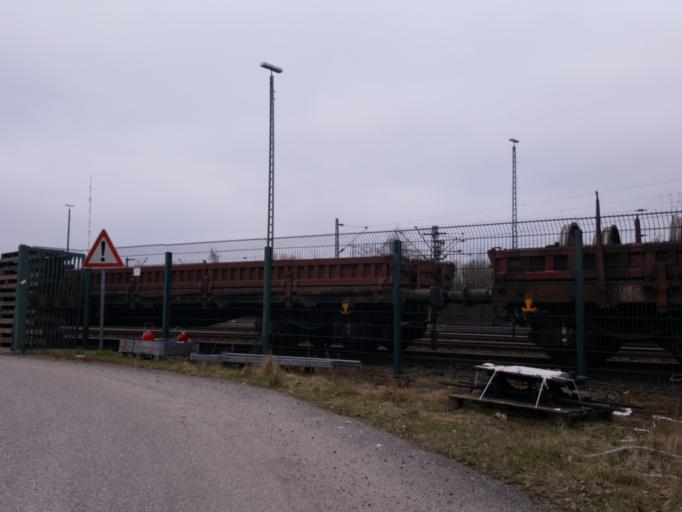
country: DE
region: Hamburg
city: Wandsbek
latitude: 53.5059
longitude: 10.1134
